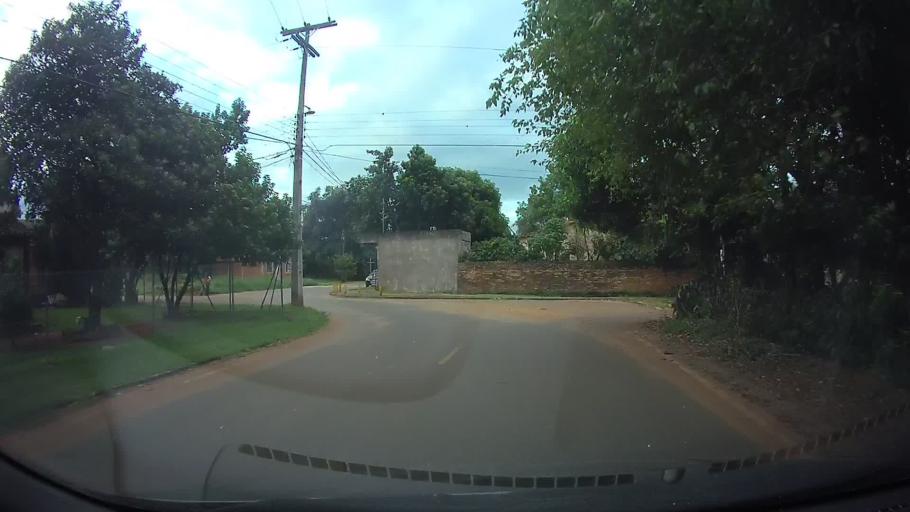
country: PY
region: Central
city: San Lorenzo
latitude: -25.2869
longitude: -57.4869
